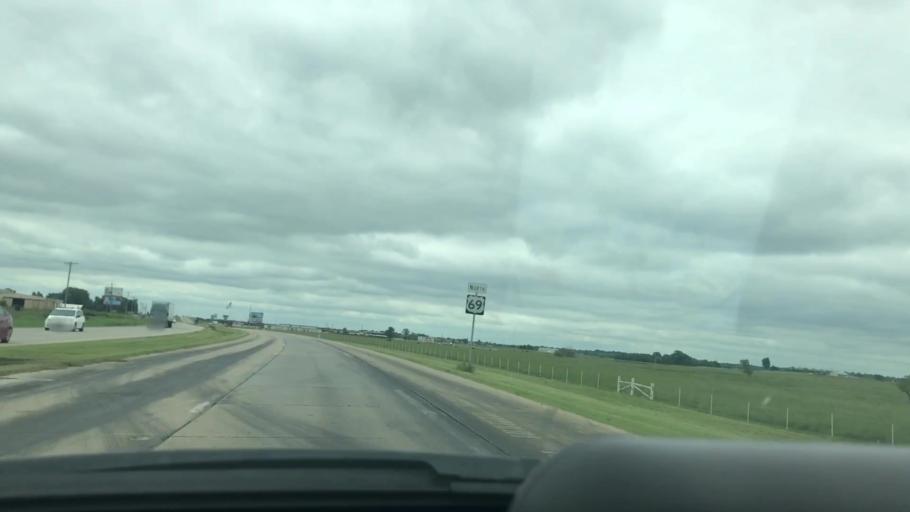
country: US
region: Oklahoma
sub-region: Craig County
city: Vinita
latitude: 36.5465
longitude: -95.2204
